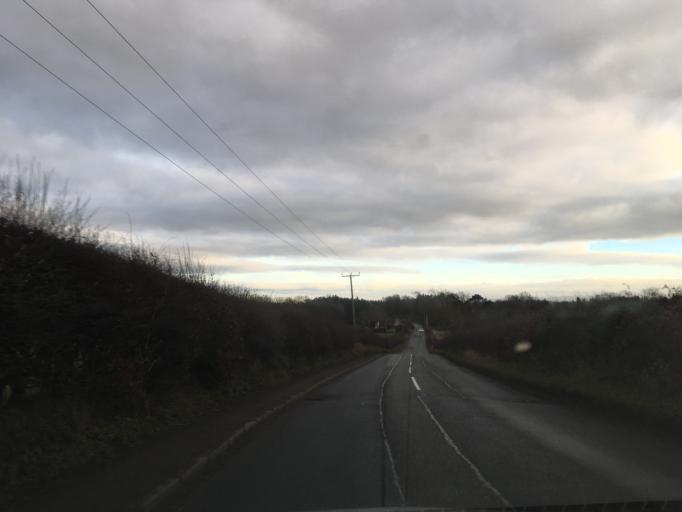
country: GB
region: Scotland
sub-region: Midlothian
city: Penicuik
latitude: 55.8650
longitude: -3.2101
